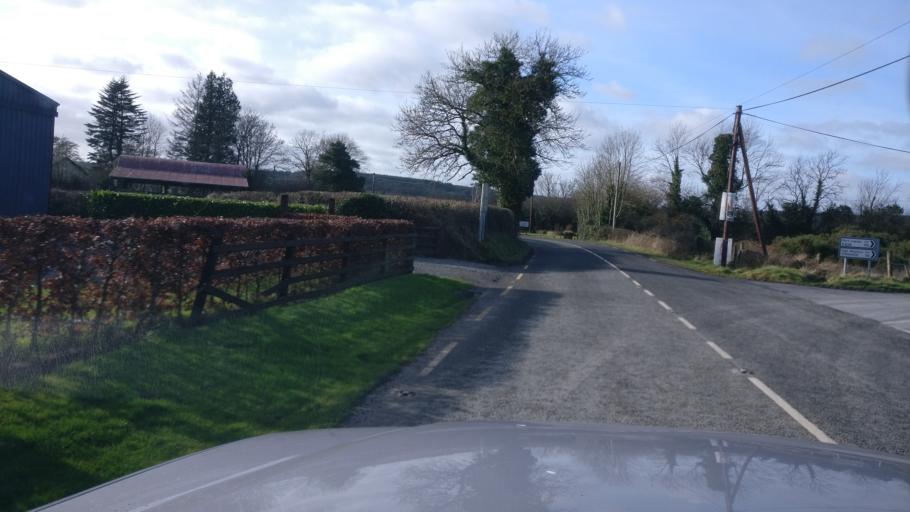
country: IE
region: Leinster
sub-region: Kilkenny
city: Castlecomer
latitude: 52.8899
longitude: -7.1635
